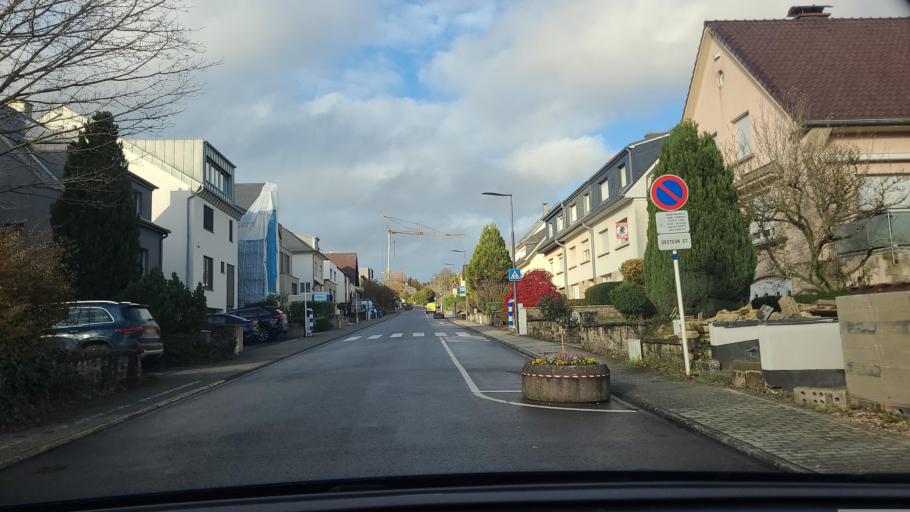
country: LU
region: Luxembourg
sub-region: Canton de Luxembourg
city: Strassen
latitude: 49.6227
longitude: 6.0698
